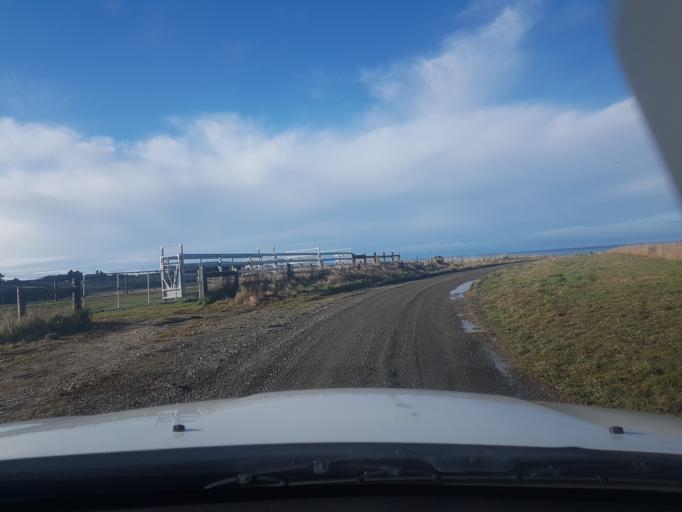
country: NZ
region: Canterbury
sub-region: Timaru District
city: Timaru
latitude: -44.4636
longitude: 171.2367
